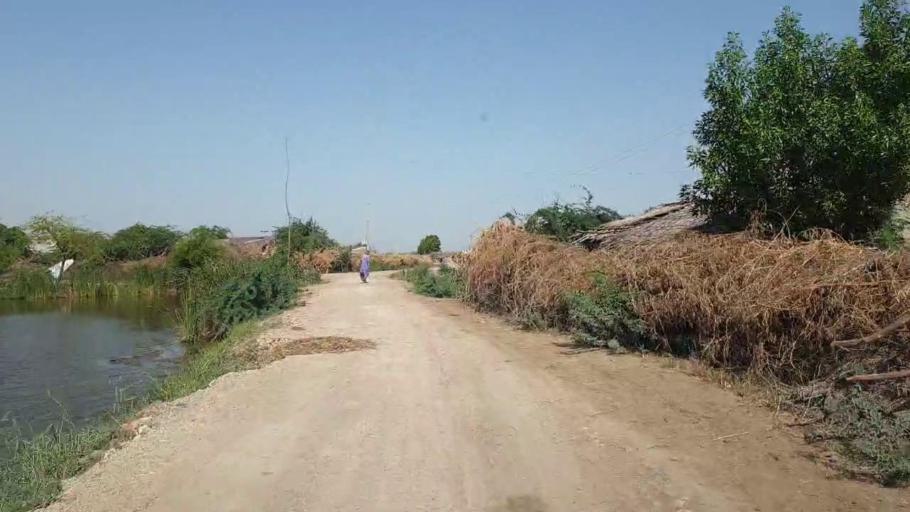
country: PK
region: Sindh
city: Tando Bago
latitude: 24.7542
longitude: 69.0278
